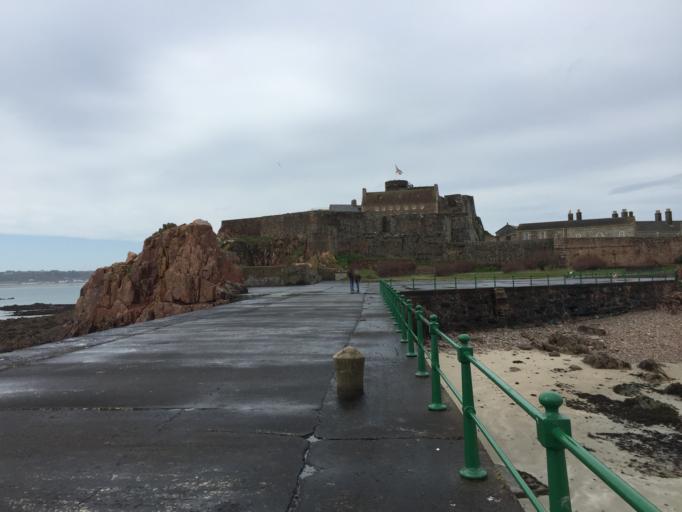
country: JE
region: St Helier
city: Saint Helier
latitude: 49.1743
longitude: -2.1255
